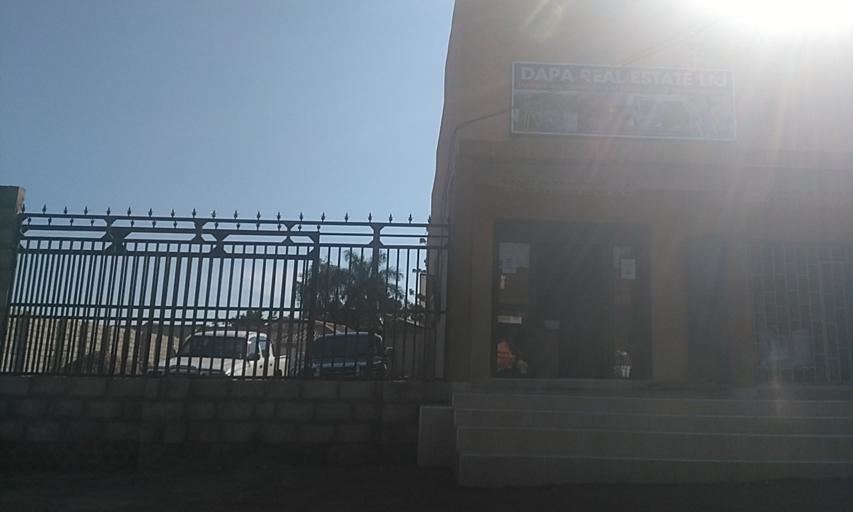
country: UG
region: Central Region
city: Kampala Central Division
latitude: 0.3210
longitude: 32.5455
